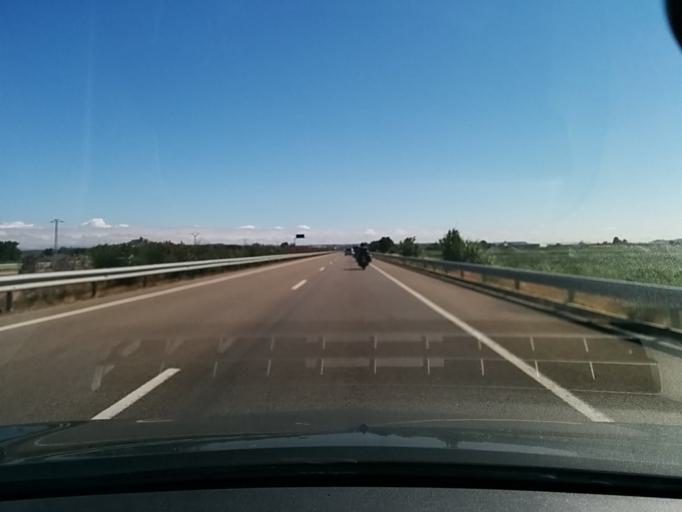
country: ES
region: Aragon
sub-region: Provincia de Huesca
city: Almudebar
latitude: 42.0245
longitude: -0.6018
